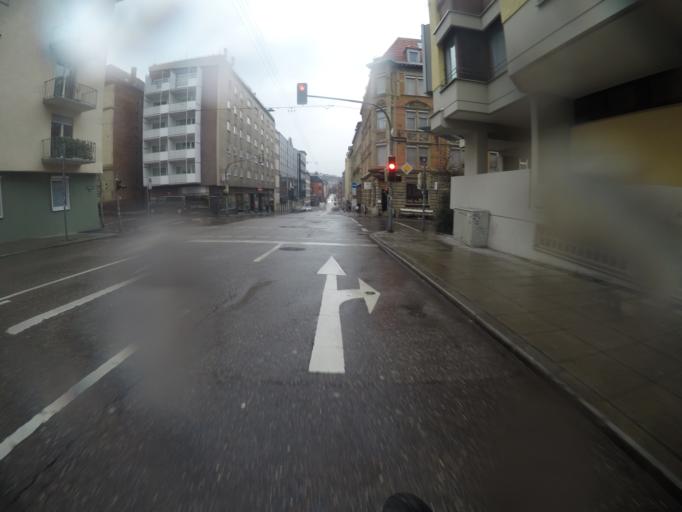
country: DE
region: Baden-Wuerttemberg
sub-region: Regierungsbezirk Stuttgart
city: Stuttgart
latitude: 48.7691
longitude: 9.1592
